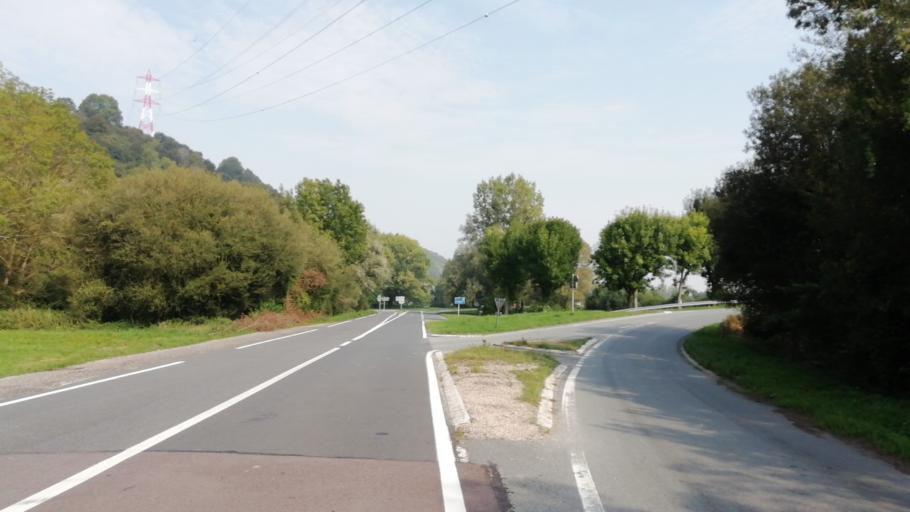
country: FR
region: Haute-Normandie
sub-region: Departement de la Seine-Maritime
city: Saint-Romain-de-Colbosc
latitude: 49.4838
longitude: 0.3550
